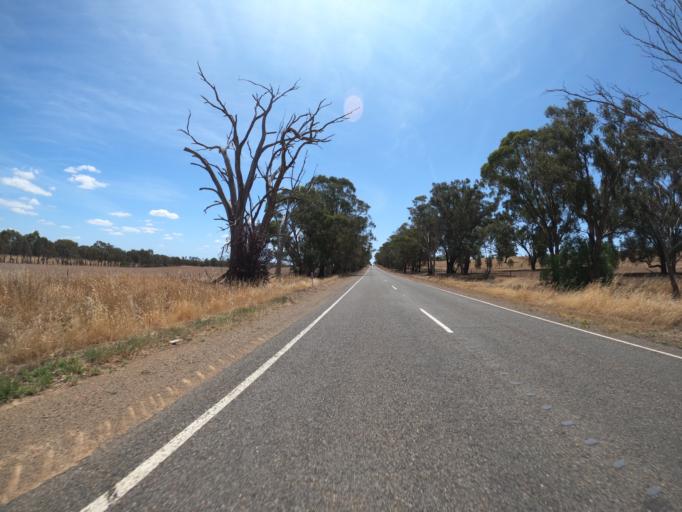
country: AU
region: Victoria
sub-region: Benalla
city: Benalla
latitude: -36.3542
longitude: 145.9645
